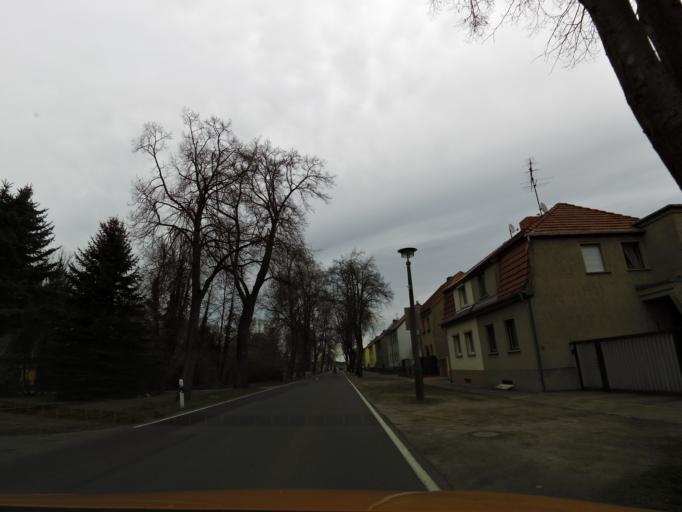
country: DE
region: Brandenburg
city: Belzig
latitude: 52.1477
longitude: 12.5990
